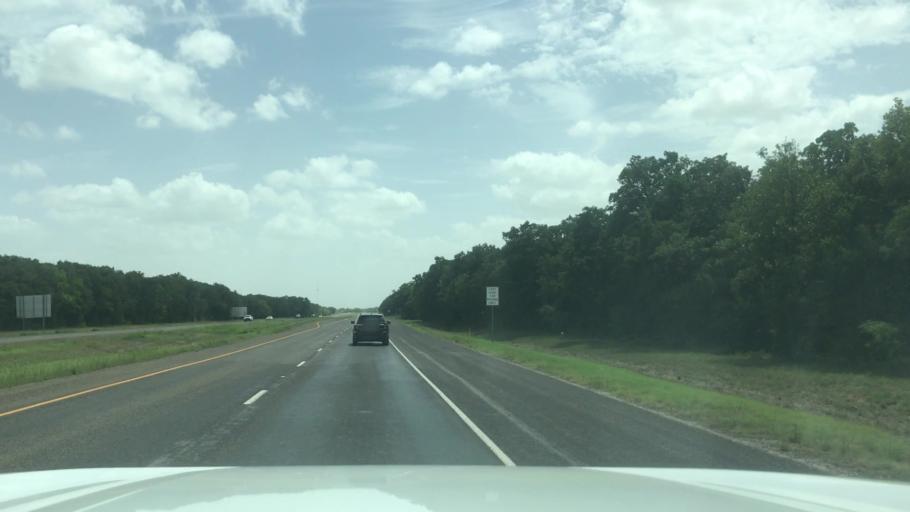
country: US
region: Texas
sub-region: Falls County
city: Marlin
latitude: 31.2973
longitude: -96.8750
